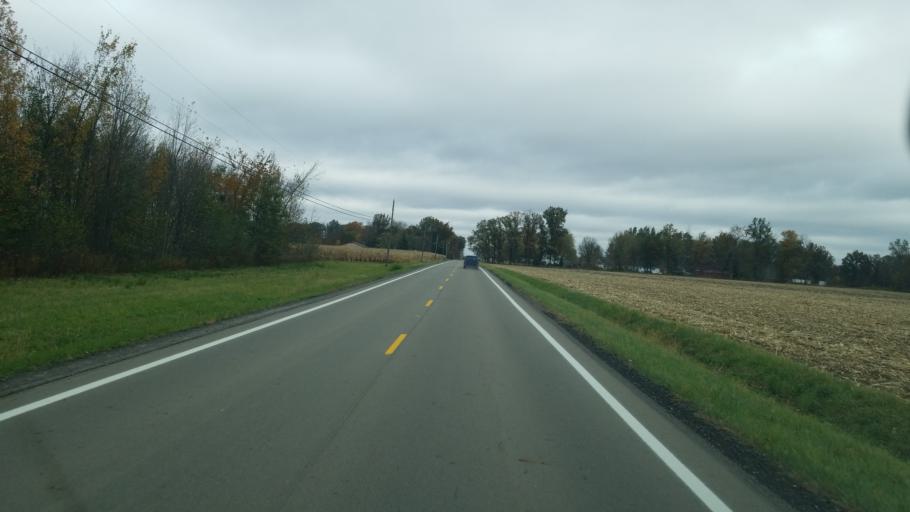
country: US
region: Ohio
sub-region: Crawford County
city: Galion
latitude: 40.8038
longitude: -82.8566
